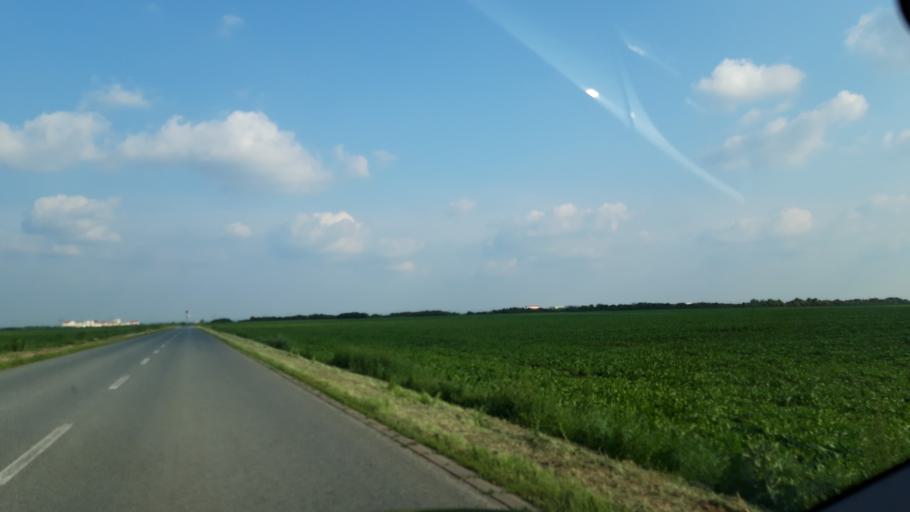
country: RS
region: Autonomna Pokrajina Vojvodina
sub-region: Sremski Okrug
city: Ingija
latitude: 45.0802
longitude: 20.1186
